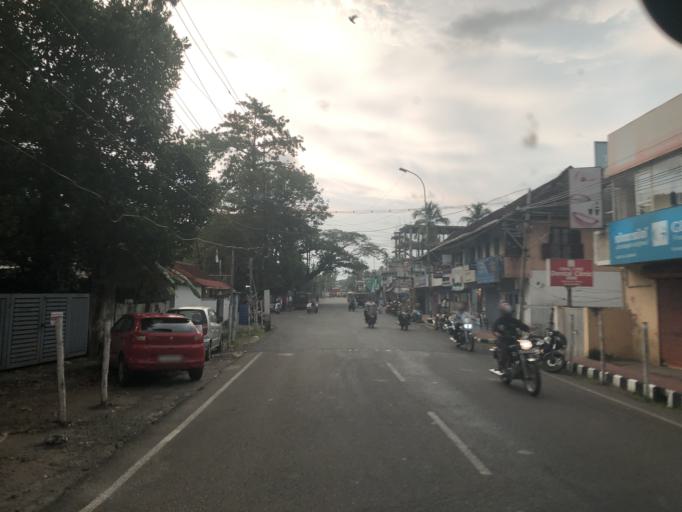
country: IN
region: Kerala
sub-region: Ernakulam
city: Cochin
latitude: 9.9520
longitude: 76.2535
